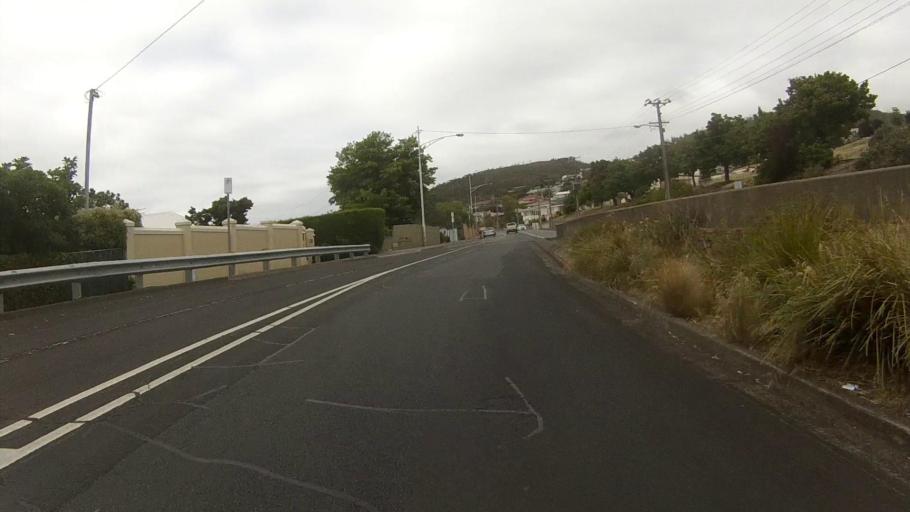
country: AU
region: Tasmania
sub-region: Kingborough
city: Taroona
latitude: -42.9147
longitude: 147.3592
